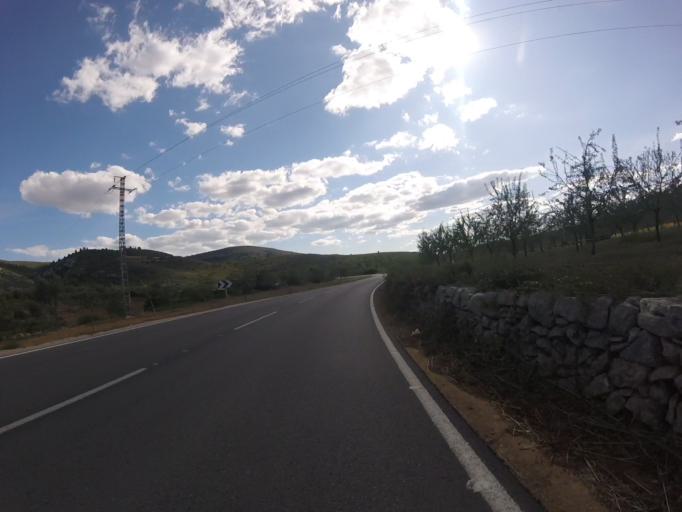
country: ES
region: Valencia
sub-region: Provincia de Castello
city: Cuevas de Vinroma
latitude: 40.3019
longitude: 0.1654
